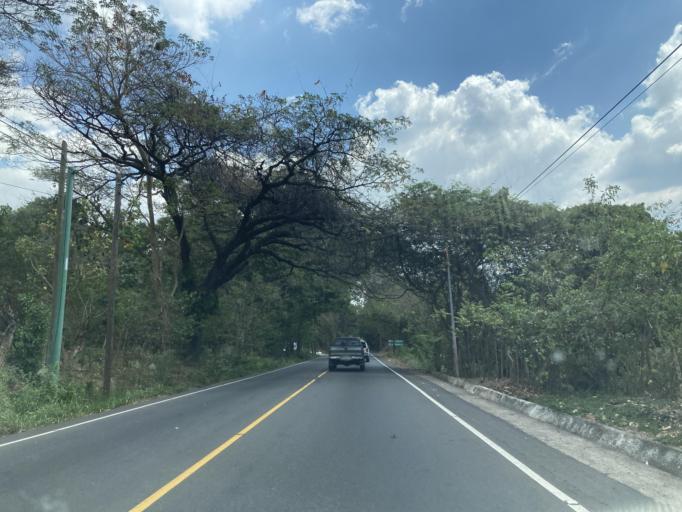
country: GT
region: Santa Rosa
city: Guazacapan
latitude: 14.0715
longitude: -90.4245
